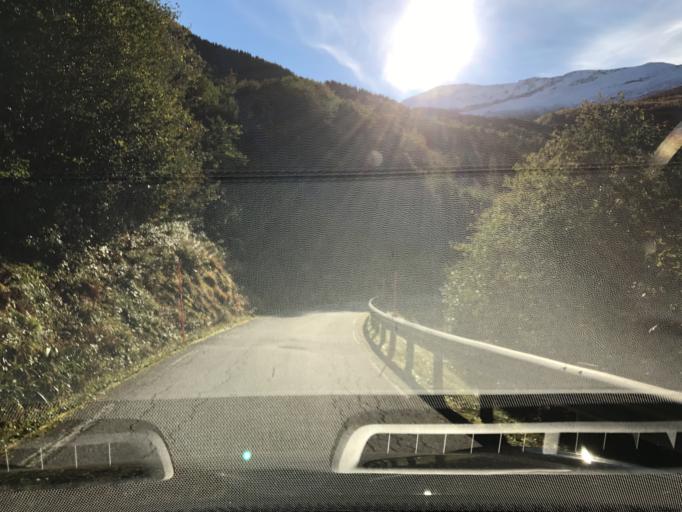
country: NO
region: More og Romsdal
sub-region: Norddal
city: Valldal
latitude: 62.3335
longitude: 7.3891
